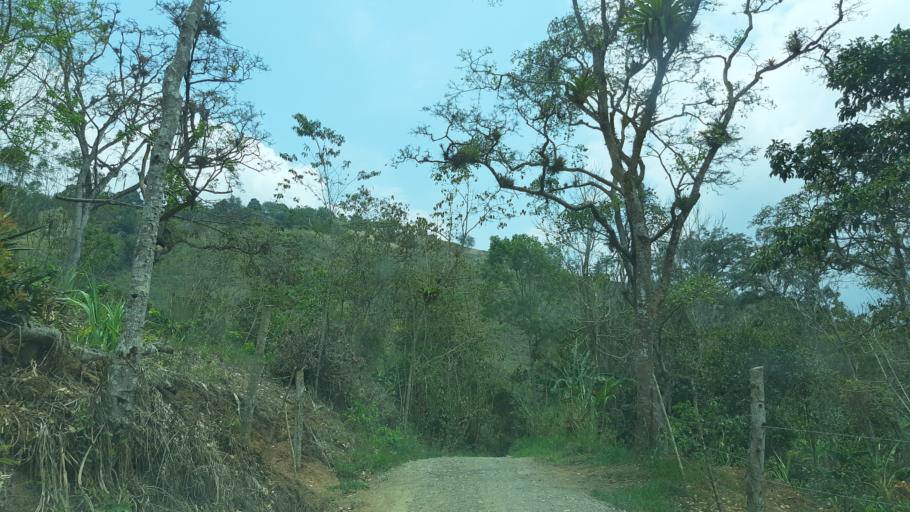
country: CO
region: Cundinamarca
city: Tenza
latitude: 5.0809
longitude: -73.4127
